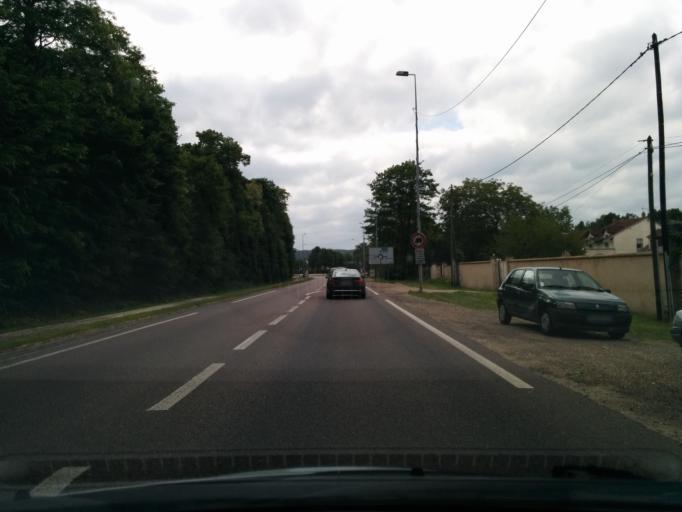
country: FR
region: Ile-de-France
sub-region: Departement des Yvelines
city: Rosny-sur-Seine
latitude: 48.9990
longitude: 1.6503
